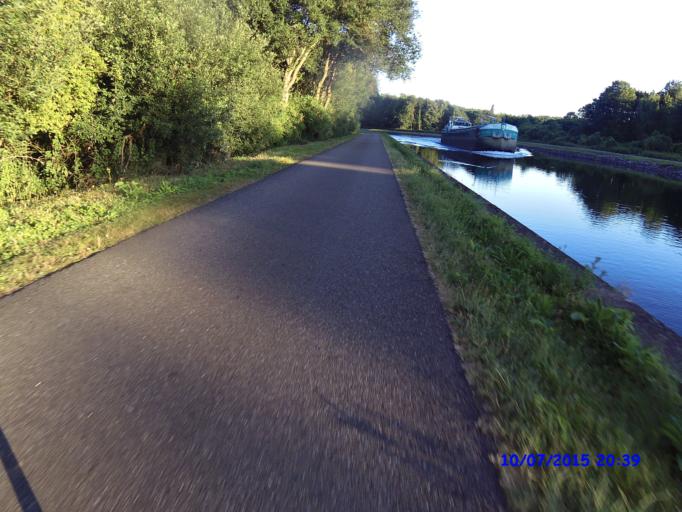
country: BE
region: Flanders
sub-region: Provincie Antwerpen
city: Rumst
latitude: 51.0465
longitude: 4.4365
